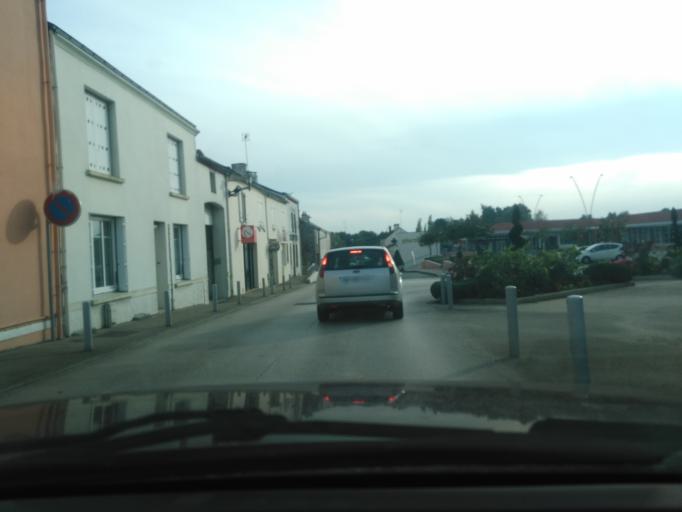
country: FR
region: Pays de la Loire
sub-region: Departement de la Vendee
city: Dompierre-sur-Yon
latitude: 46.7388
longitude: -1.3847
